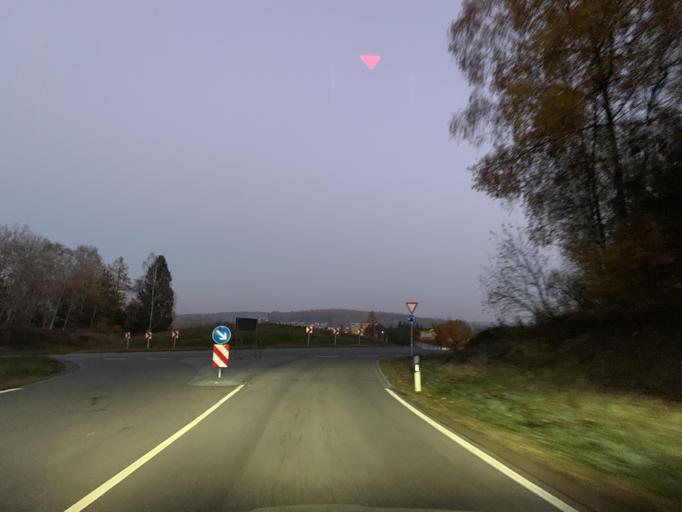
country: DE
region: Bavaria
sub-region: Upper Palatinate
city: Bruck in der Oberpfalz
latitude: 49.2507
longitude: 12.2954
